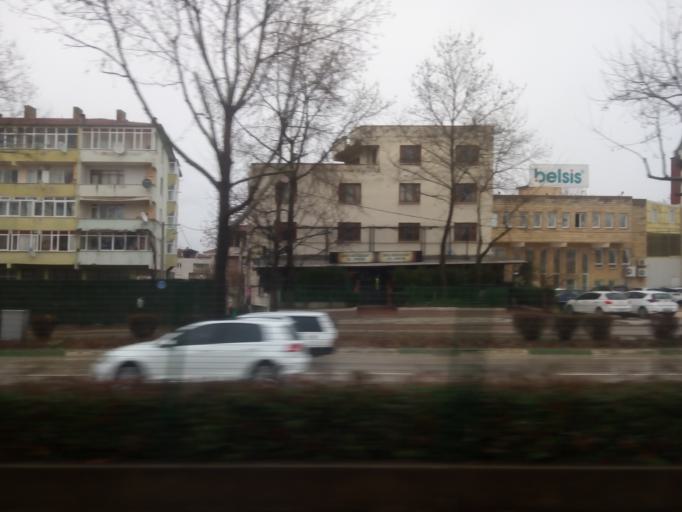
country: TR
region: Bursa
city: Yildirim
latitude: 40.2213
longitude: 28.9957
